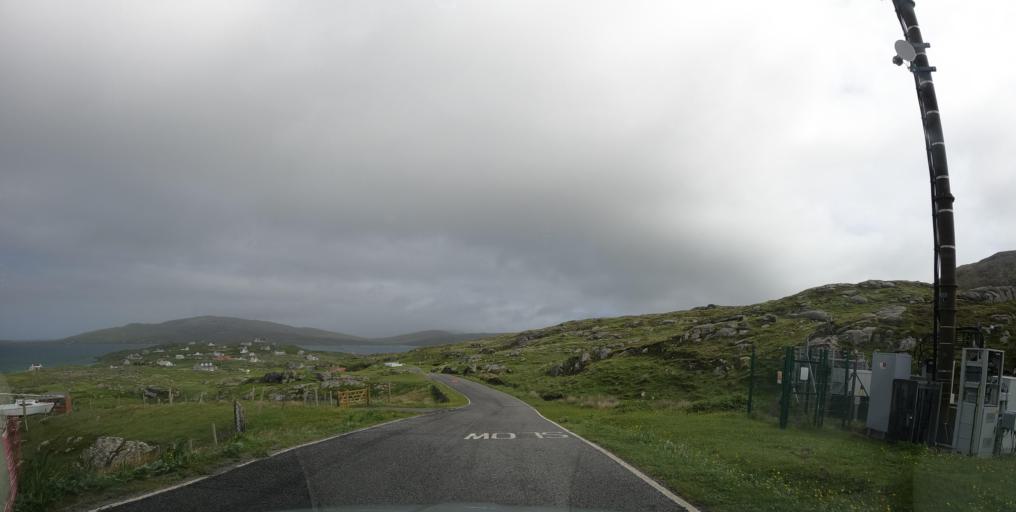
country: GB
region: Scotland
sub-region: Eilean Siar
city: Isle of South Uist
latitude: 57.0791
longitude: -7.3023
